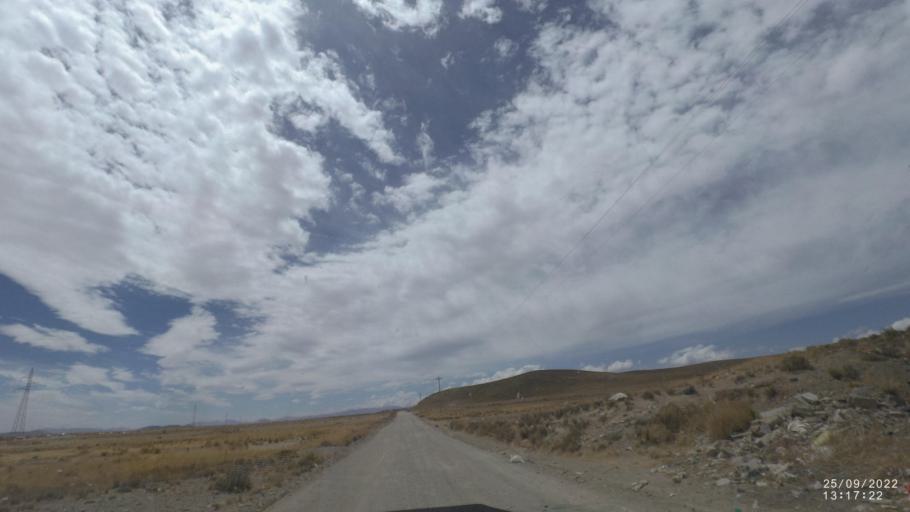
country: BO
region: Oruro
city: Oruro
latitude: -17.9097
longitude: -67.0437
